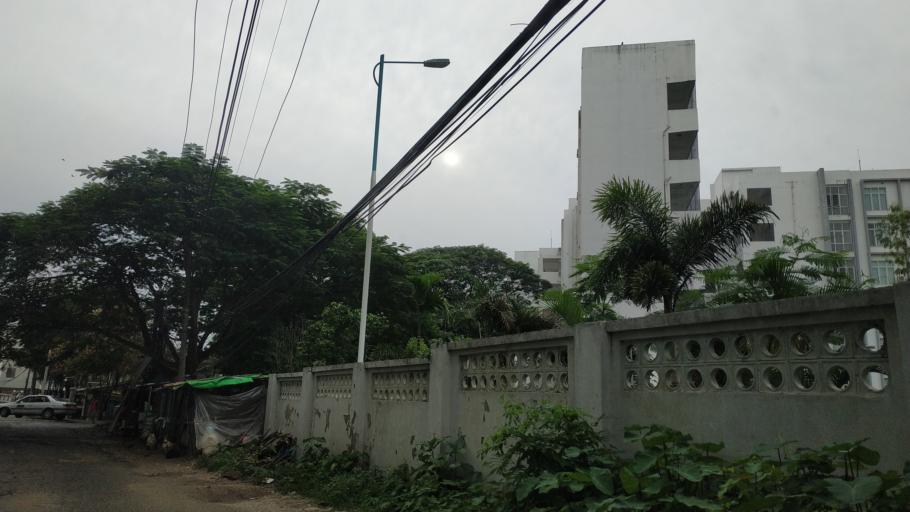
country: MM
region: Yangon
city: Yangon
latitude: 16.8481
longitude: 96.1347
